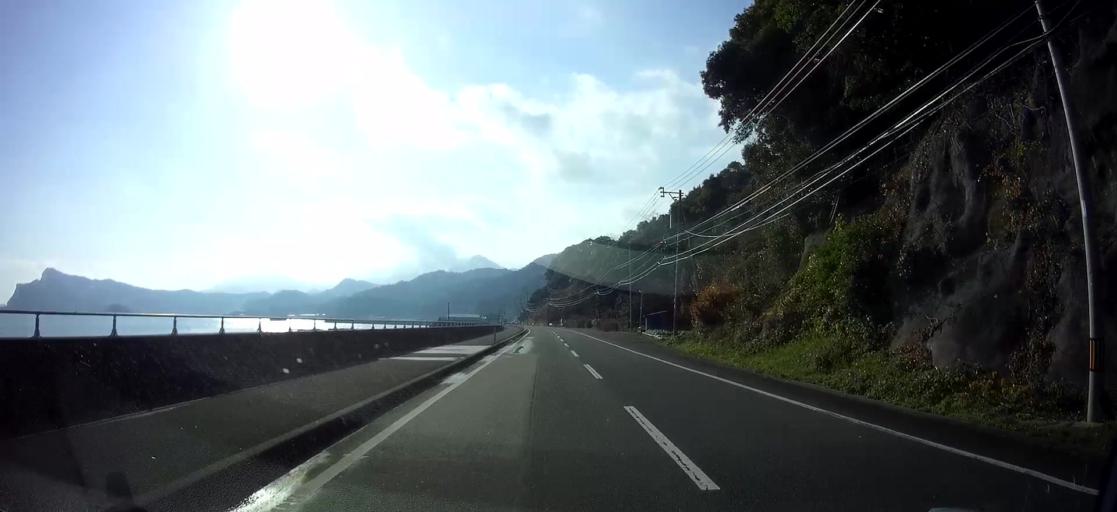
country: JP
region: Kumamoto
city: Yatsushiro
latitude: 32.4541
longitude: 130.4261
